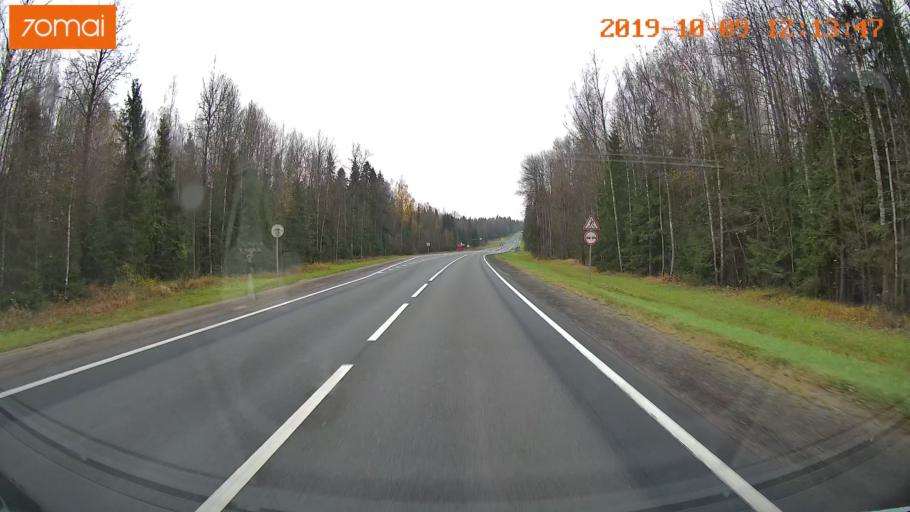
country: RU
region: Jaroslavl
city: Prechistoye
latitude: 58.5052
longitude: 40.3438
